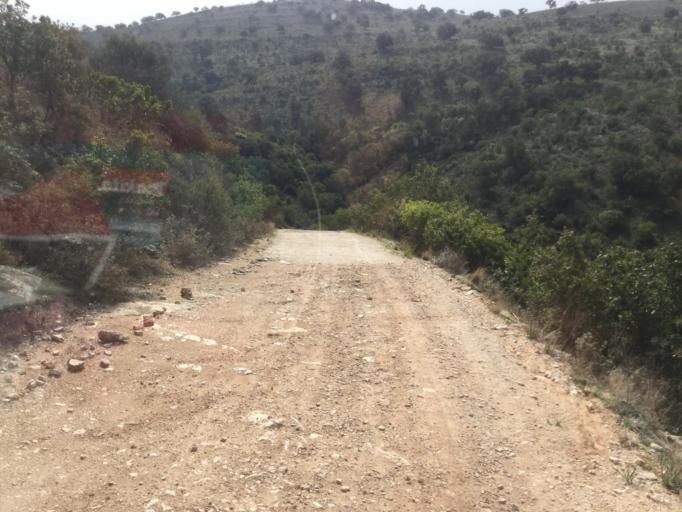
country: GR
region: West Greece
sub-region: Nomos Achaias
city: Lapas
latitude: 38.1747
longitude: 21.3750
